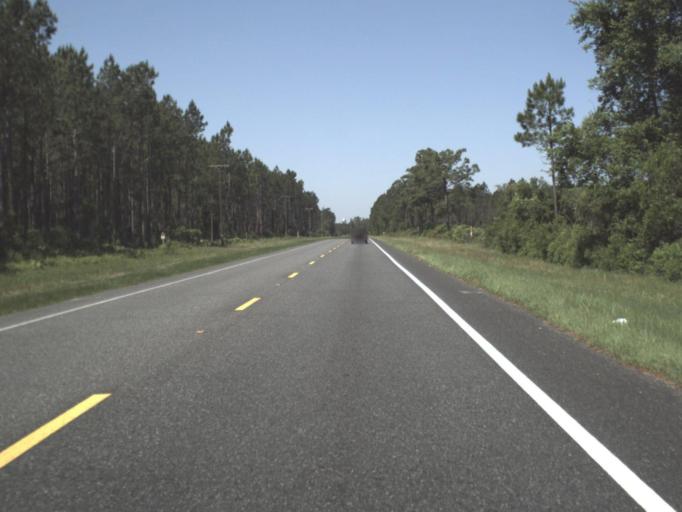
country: US
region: Florida
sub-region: Union County
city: Lake Butler
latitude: 30.2234
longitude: -82.3480
